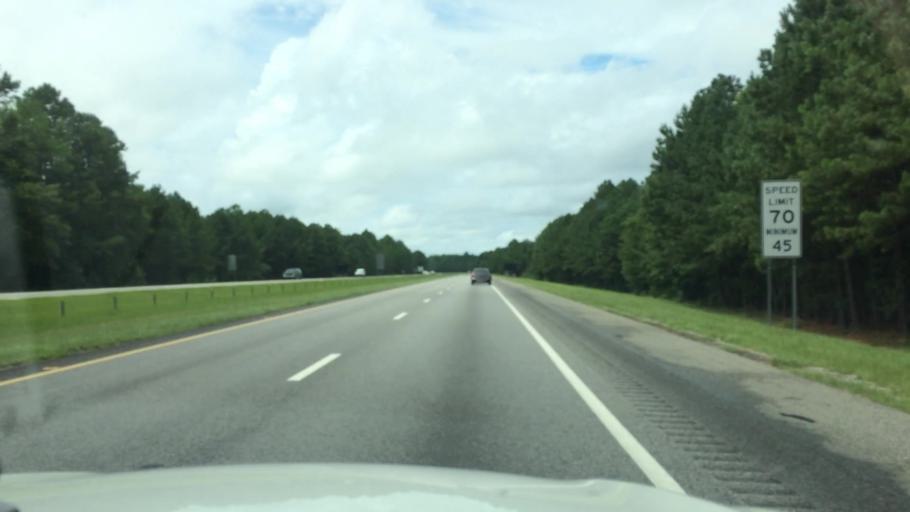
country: US
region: South Carolina
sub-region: Florence County
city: Florence
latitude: 34.2010
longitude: -79.8615
